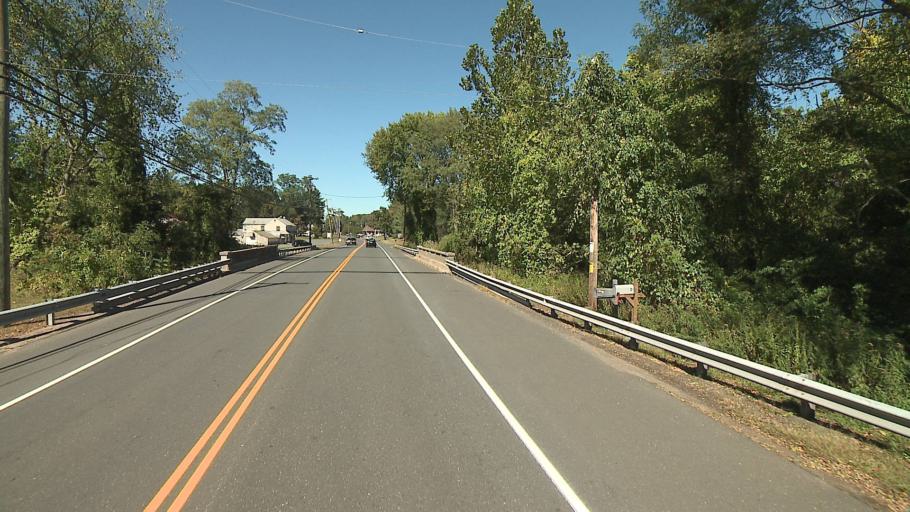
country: US
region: Connecticut
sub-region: Hartford County
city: Salmon Brook
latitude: 41.9636
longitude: -72.7906
